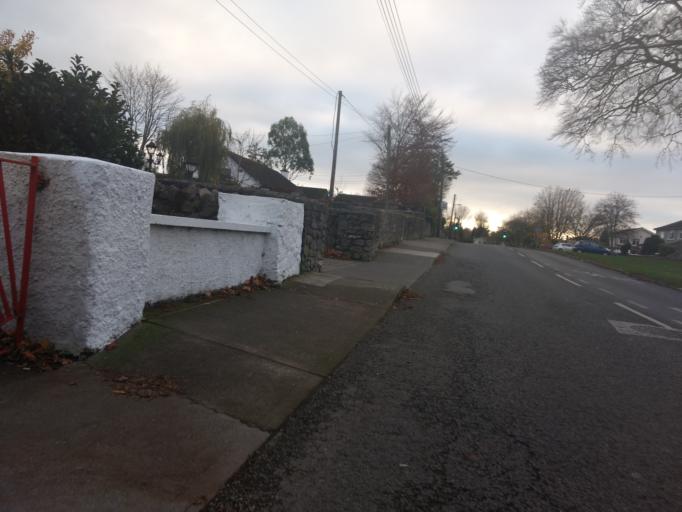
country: IE
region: Leinster
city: Malahide
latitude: 53.4492
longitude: -6.1758
